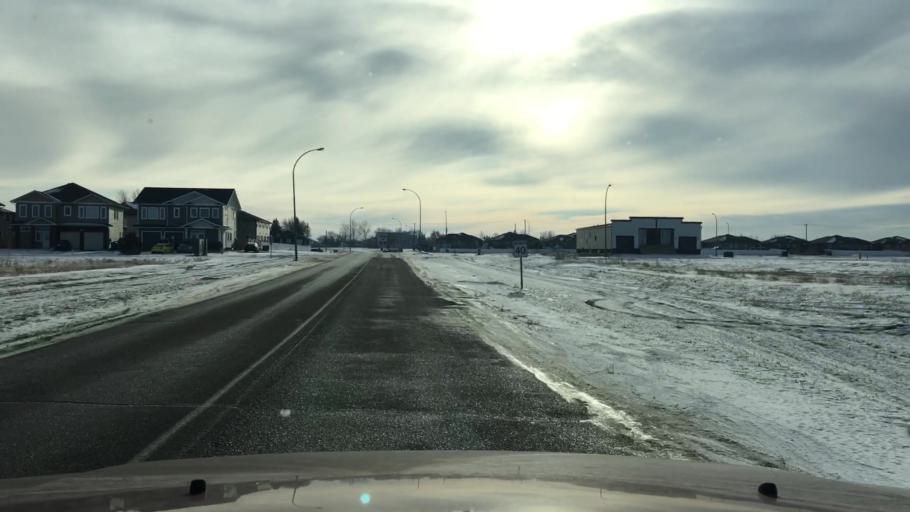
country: CA
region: Saskatchewan
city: Pilot Butte
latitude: 50.4870
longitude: -104.4202
